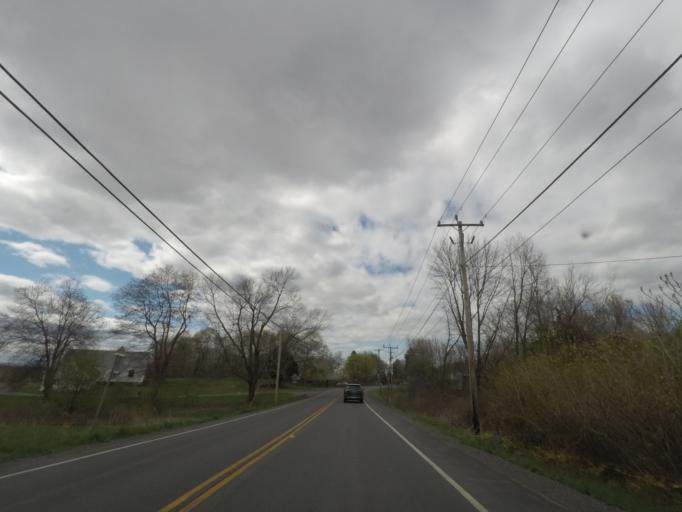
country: US
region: New York
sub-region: Columbia County
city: Chatham
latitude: 42.3606
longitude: -73.6129
